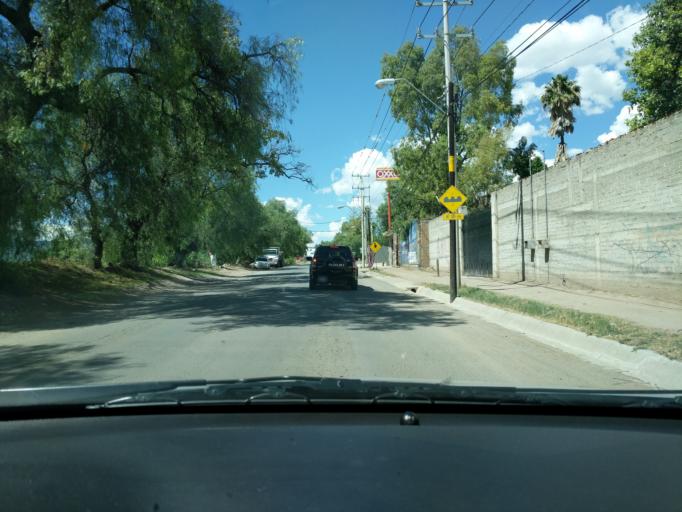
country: MX
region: Guanajuato
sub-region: Leon
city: Ladrilleras del Refugio
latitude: 21.0681
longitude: -101.5518
